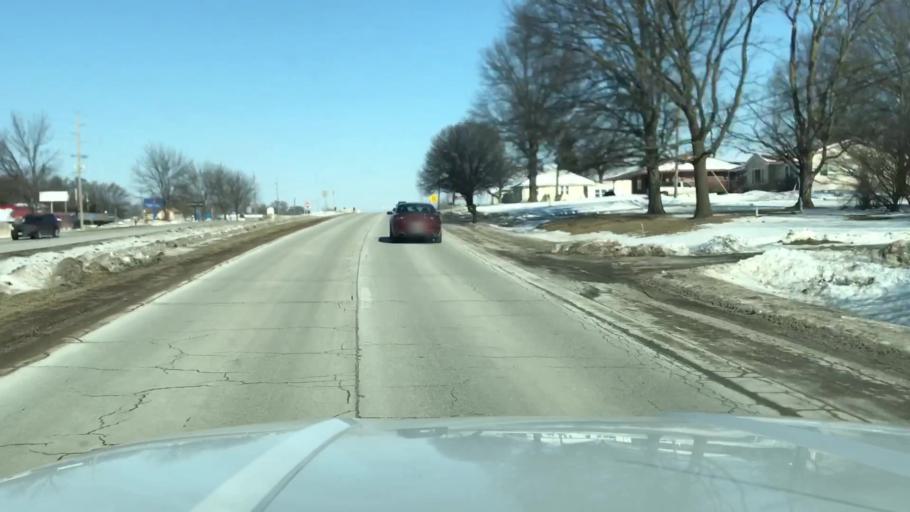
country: US
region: Missouri
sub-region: Andrew County
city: Savannah
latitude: 39.9364
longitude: -94.8218
